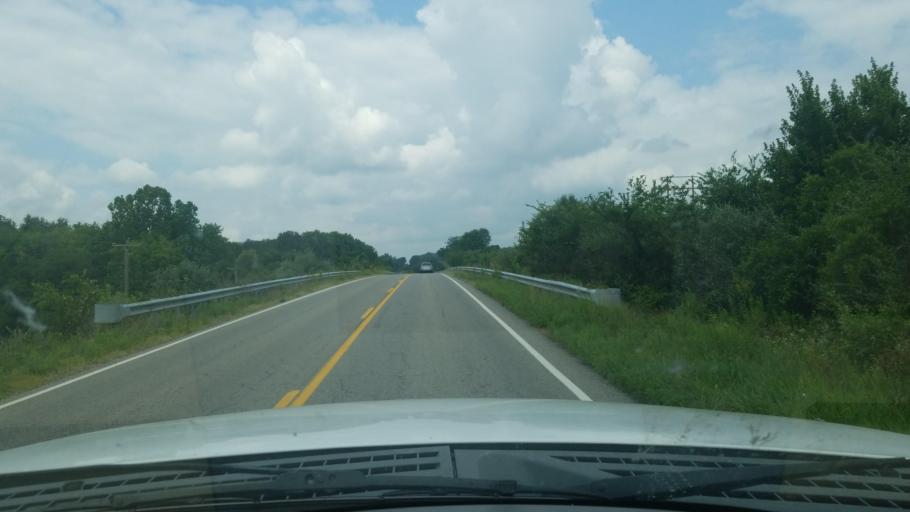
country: US
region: Illinois
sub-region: Saline County
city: Carrier Mills
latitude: 37.7488
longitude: -88.6753
